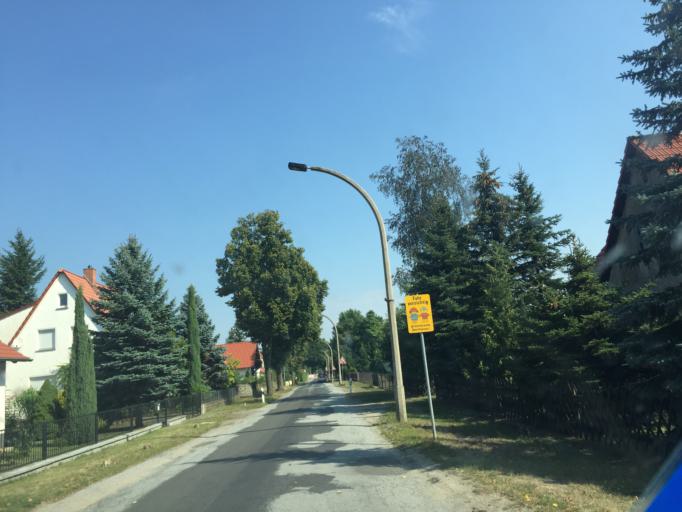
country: DE
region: Saxony
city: Uhyst
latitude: 51.3585
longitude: 14.5078
